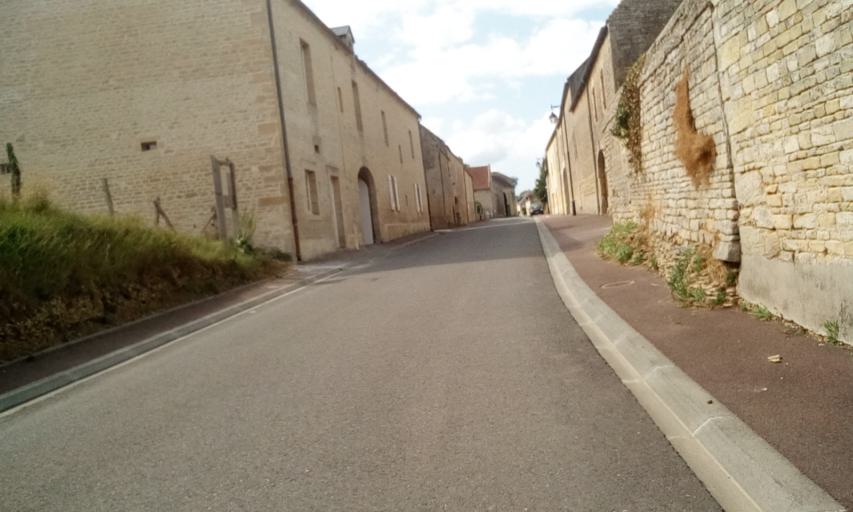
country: FR
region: Lower Normandy
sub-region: Departement du Calvados
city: Courseulles-sur-Mer
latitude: 49.3111
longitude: -0.4823
